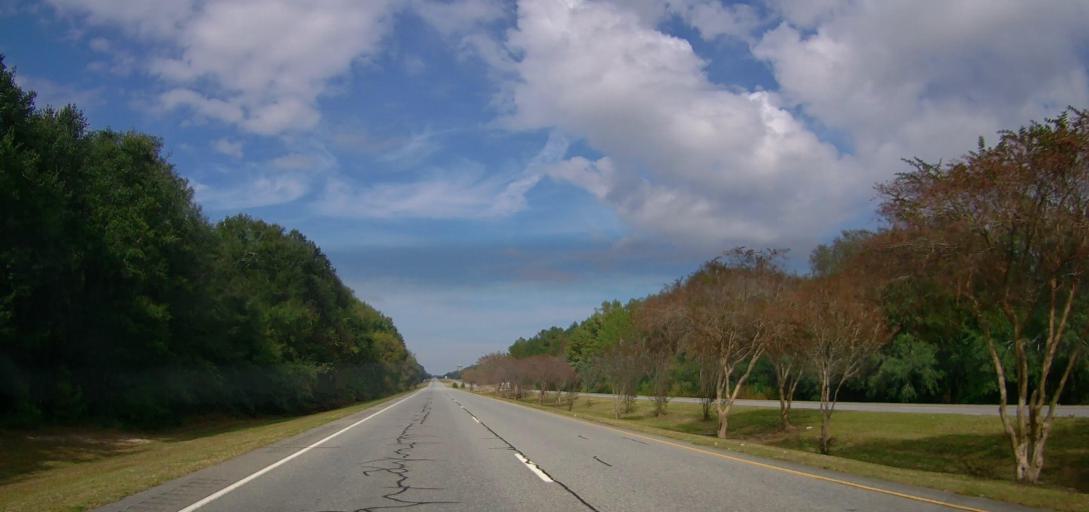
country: US
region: Georgia
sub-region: Mitchell County
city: Camilla
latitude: 31.2484
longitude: -84.1990
